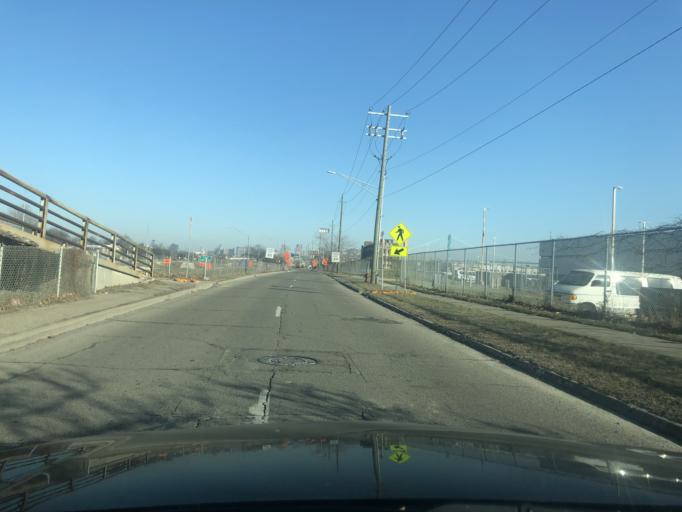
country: US
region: Michigan
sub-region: Wayne County
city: Detroit
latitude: 42.3116
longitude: -83.0950
